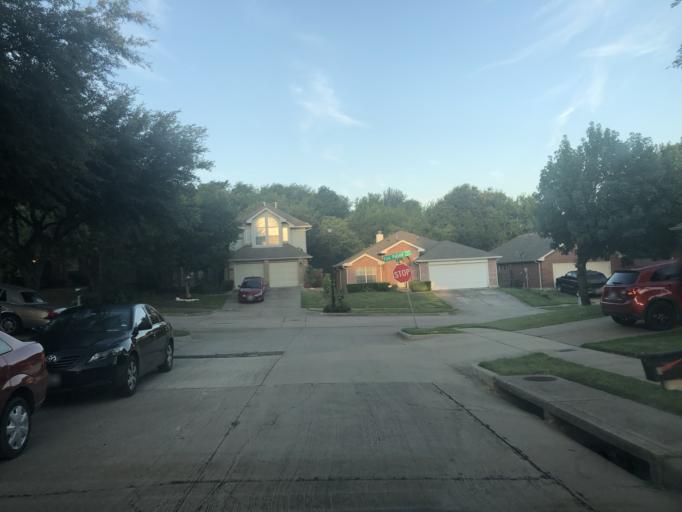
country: US
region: Texas
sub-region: Dallas County
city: Duncanville
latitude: 32.6507
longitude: -96.9699
